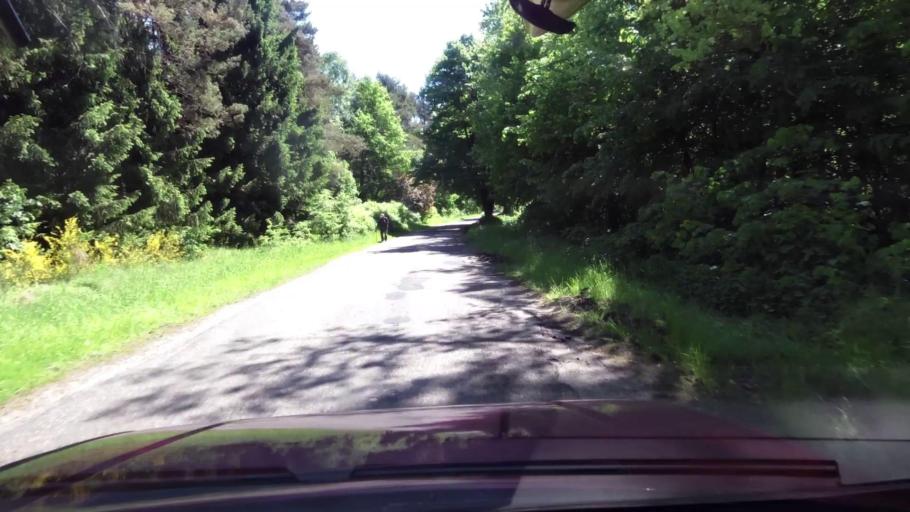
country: PL
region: West Pomeranian Voivodeship
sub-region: Powiat koszalinski
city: Bobolice
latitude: 54.0504
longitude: 16.5858
